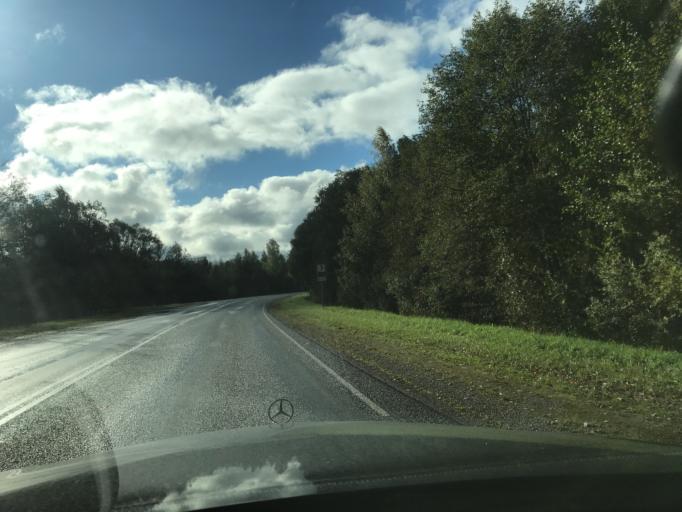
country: EE
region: Tartu
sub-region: Elva linn
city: Elva
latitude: 58.0003
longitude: 26.2682
